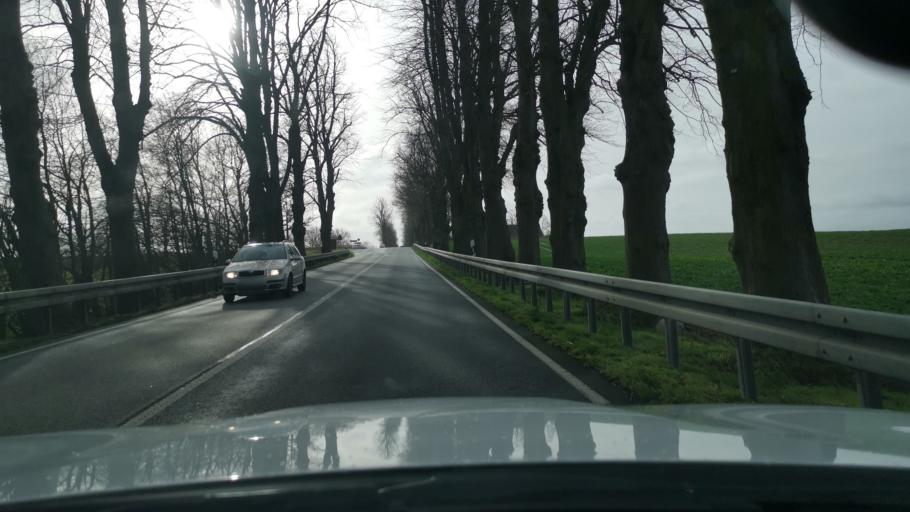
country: DE
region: Mecklenburg-Vorpommern
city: Laage
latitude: 53.9598
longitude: 12.2969
